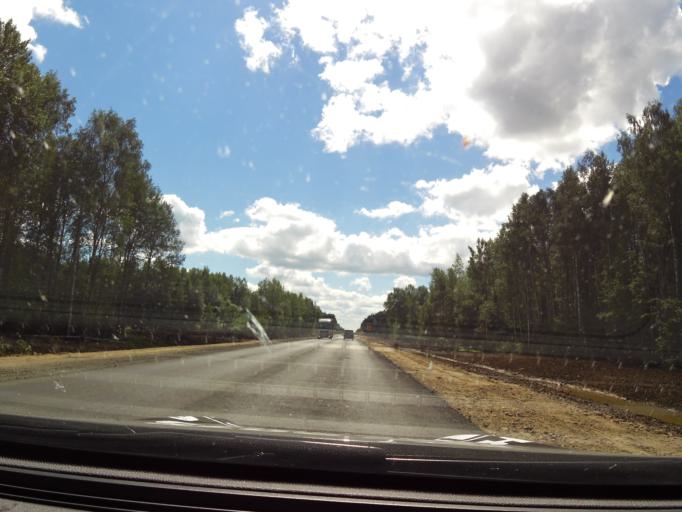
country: RU
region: Vologda
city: Molochnoye
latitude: 59.3378
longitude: 39.6803
